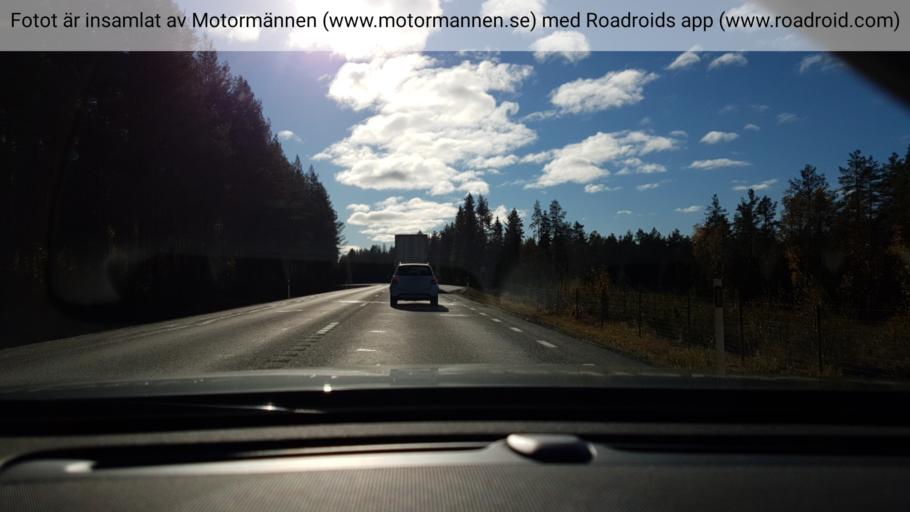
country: SE
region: Vaesterbotten
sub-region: Skelleftea Kommun
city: Burea
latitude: 64.4923
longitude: 21.2704
